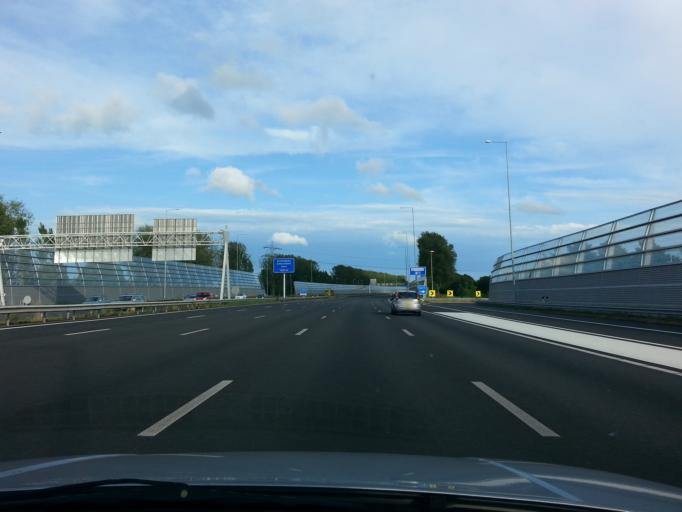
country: NL
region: North Holland
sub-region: Gemeente Diemen
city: Diemen
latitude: 52.3458
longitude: 4.9766
